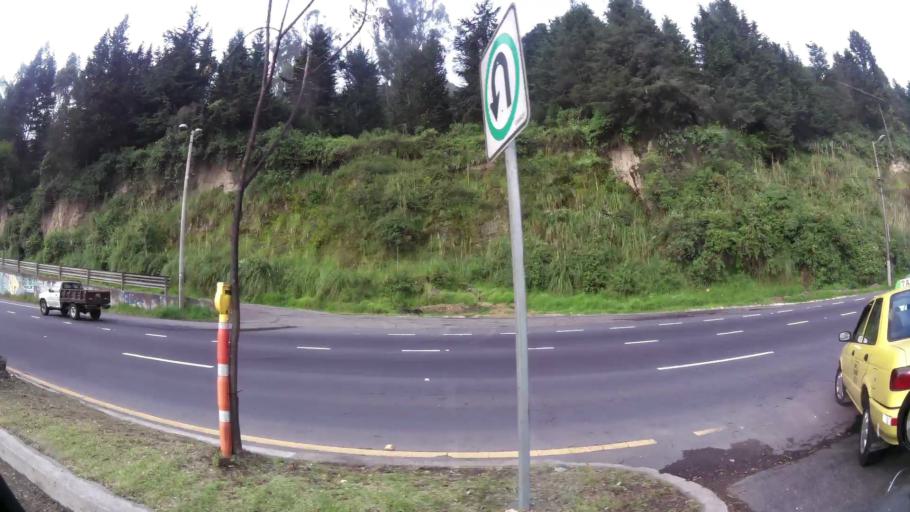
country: EC
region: Pichincha
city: Quito
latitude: -0.2444
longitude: -78.4821
